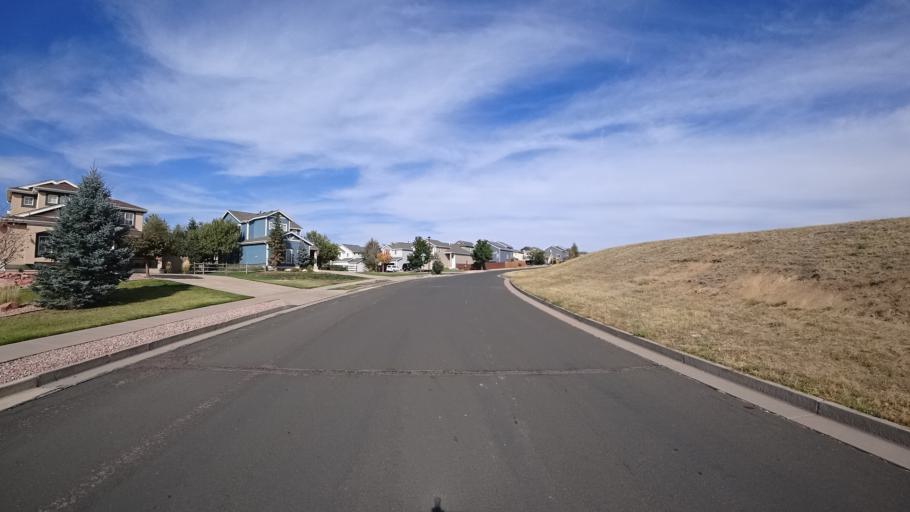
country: US
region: Colorado
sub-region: El Paso County
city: Cimarron Hills
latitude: 38.9062
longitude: -104.6905
